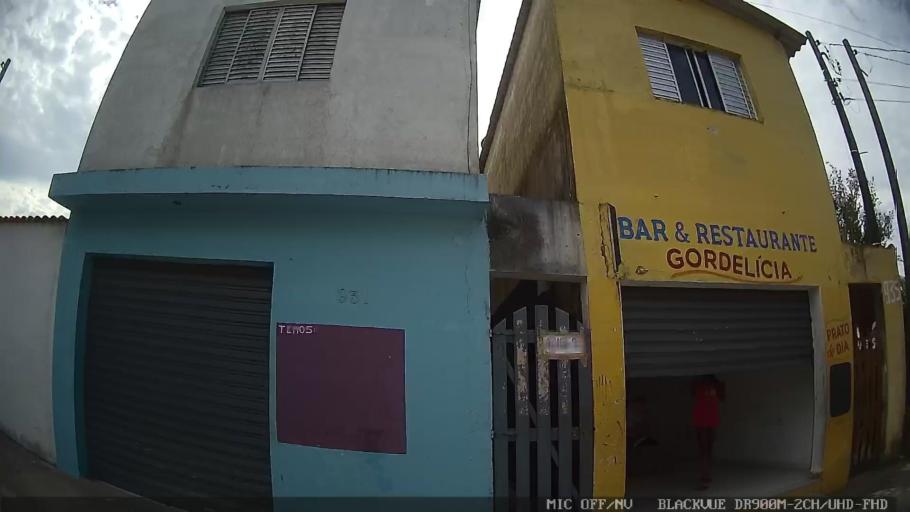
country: BR
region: Sao Paulo
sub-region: Itanhaem
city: Itanhaem
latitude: -24.1580
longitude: -46.7559
